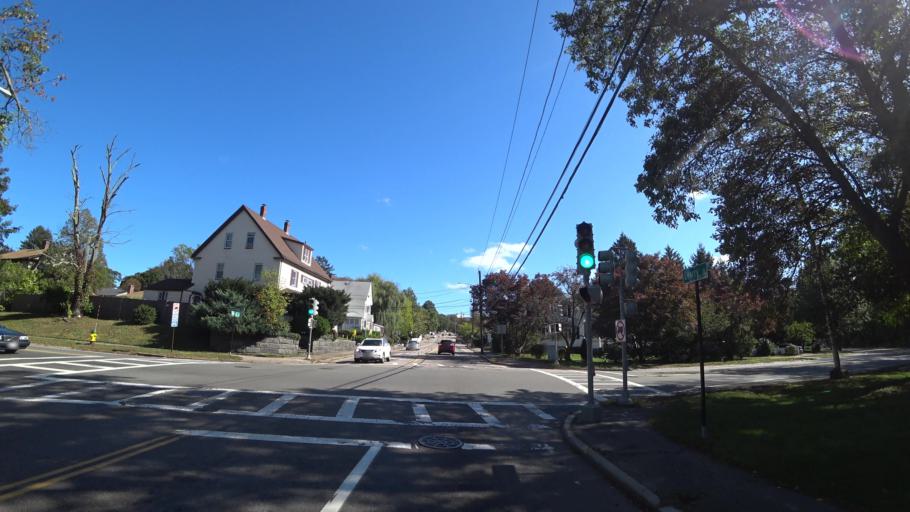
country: US
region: Massachusetts
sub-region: Norfolk County
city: Quincy
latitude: 42.2505
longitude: -71.0304
